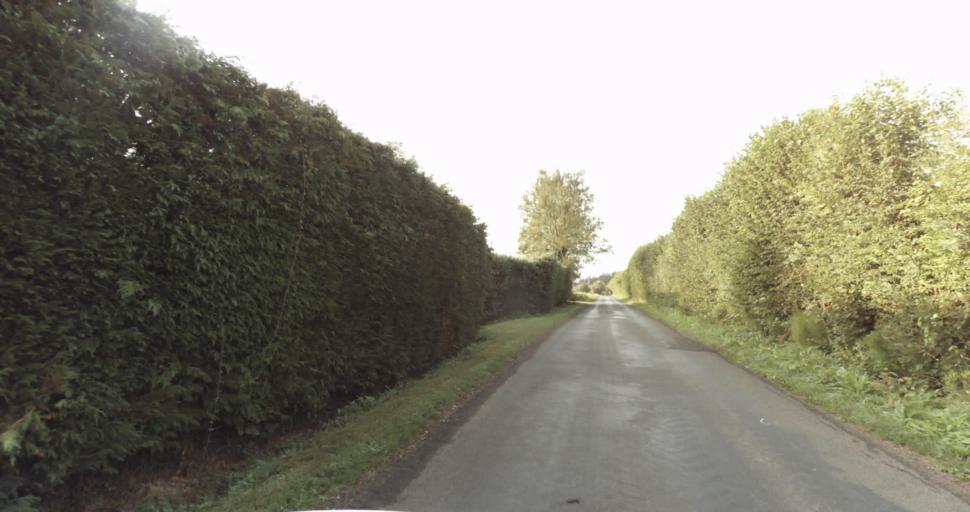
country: FR
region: Lower Normandy
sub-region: Departement de l'Orne
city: Vimoutiers
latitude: 48.9249
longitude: 0.2651
